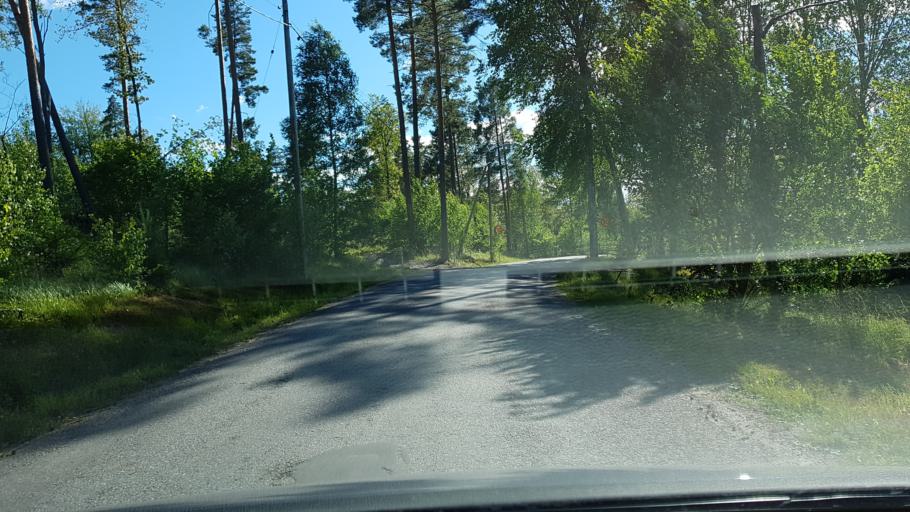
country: SE
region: Stockholm
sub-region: Upplands-Bro Kommun
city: Kungsaengen
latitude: 59.4850
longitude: 17.8029
